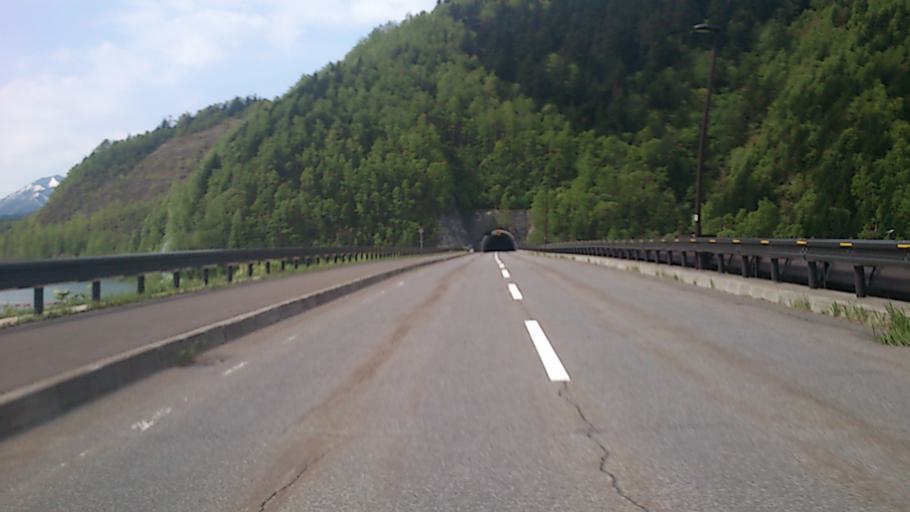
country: JP
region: Hokkaido
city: Kamikawa
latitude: 43.6771
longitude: 143.0369
